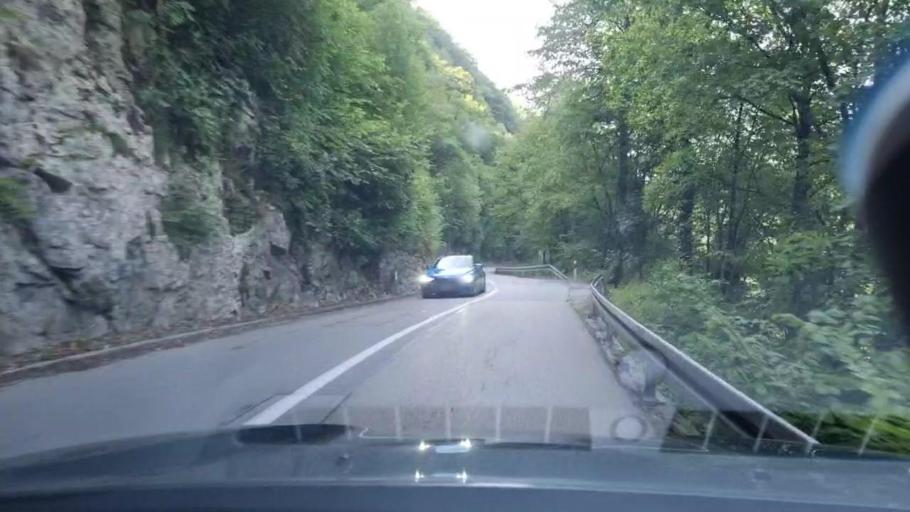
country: BA
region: Federation of Bosnia and Herzegovina
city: Stijena
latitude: 44.8912
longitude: 16.0503
